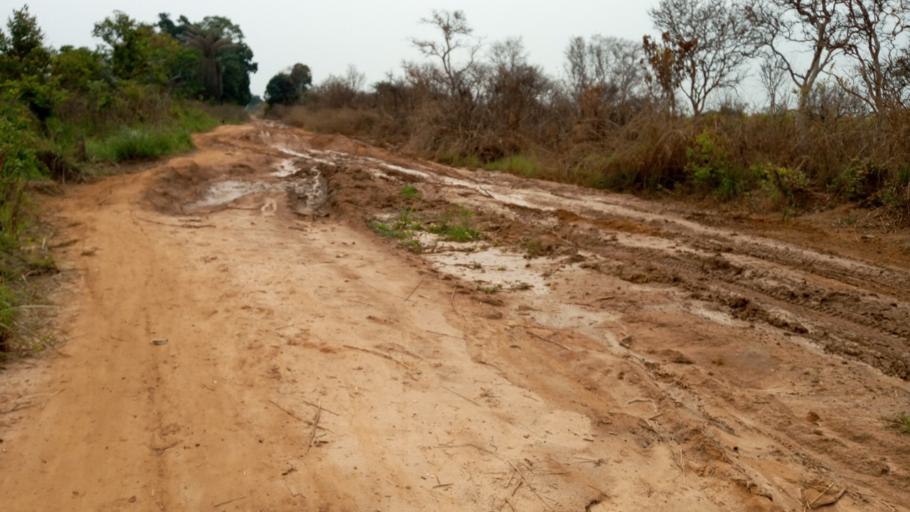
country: CD
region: Bandundu
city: Bandundu
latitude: -3.4517
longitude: 17.7575
